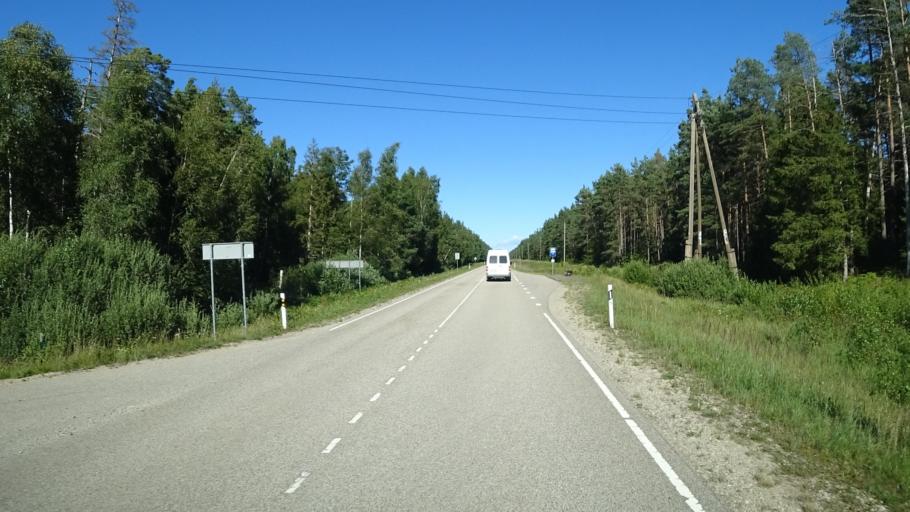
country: LV
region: Dundaga
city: Dundaga
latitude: 57.7254
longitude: 22.4916
